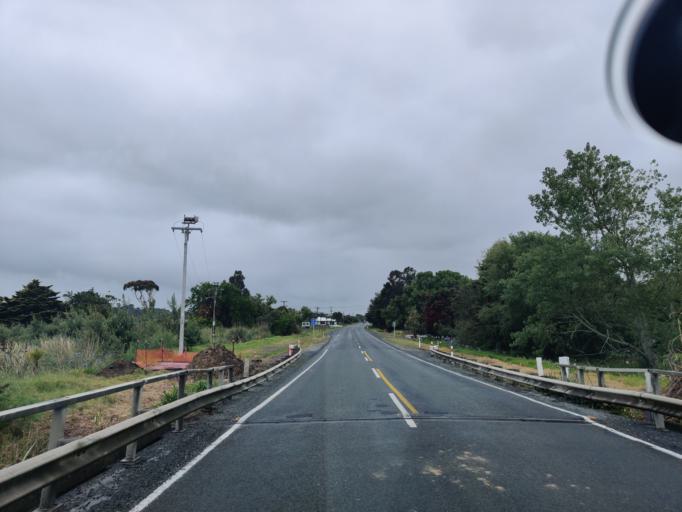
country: NZ
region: Northland
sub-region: Kaipara District
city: Dargaville
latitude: -35.9413
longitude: 173.8855
